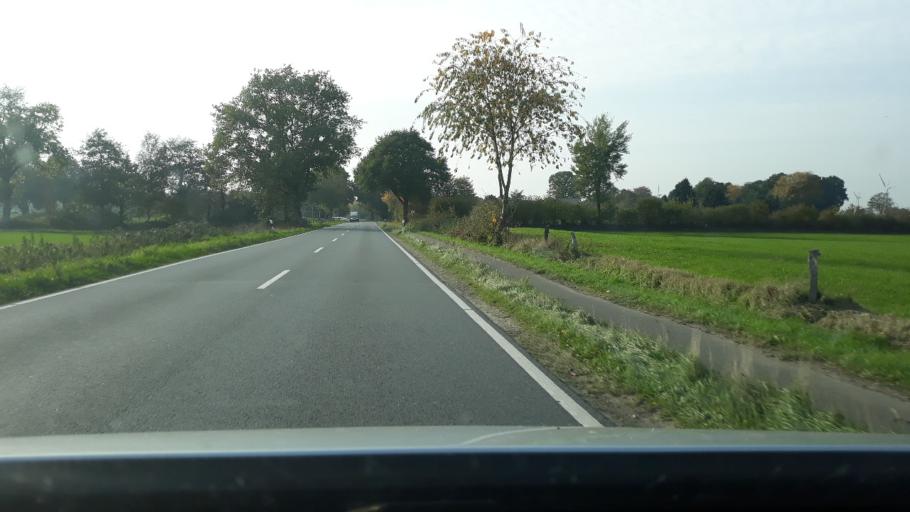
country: DE
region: Schleswig-Holstein
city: Owschlag
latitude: 54.4022
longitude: 9.5965
